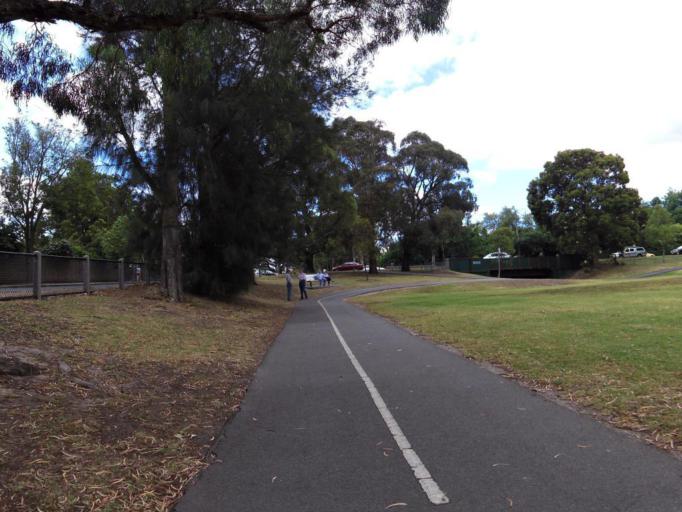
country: AU
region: Victoria
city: Balwyn
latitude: -37.8213
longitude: 145.0675
